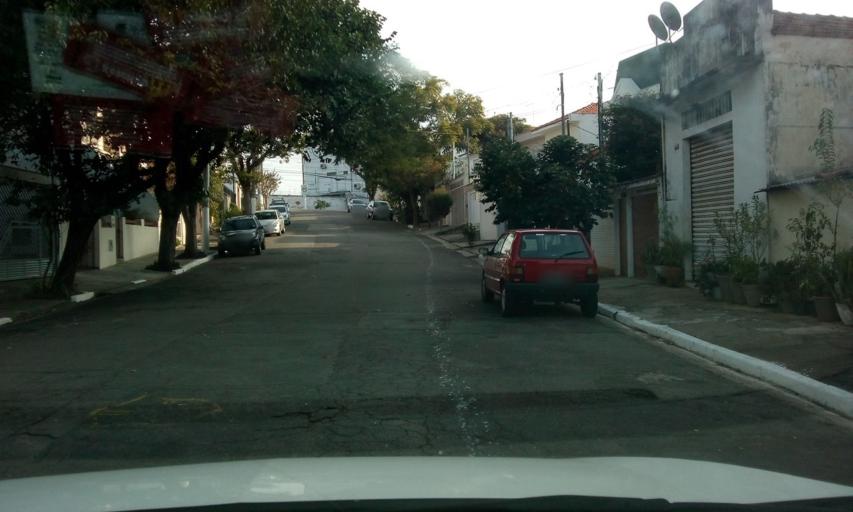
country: BR
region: Sao Paulo
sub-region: Sao Paulo
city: Sao Paulo
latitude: -23.6119
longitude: -46.6547
